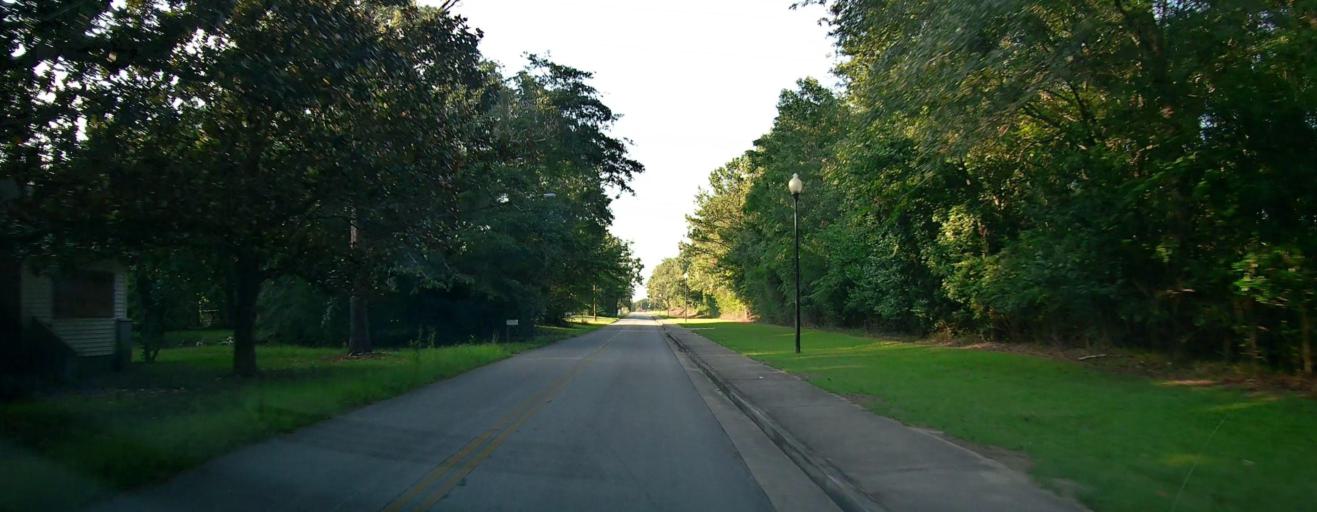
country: US
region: Georgia
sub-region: Crawford County
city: Roberta
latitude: 32.7137
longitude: -84.0093
